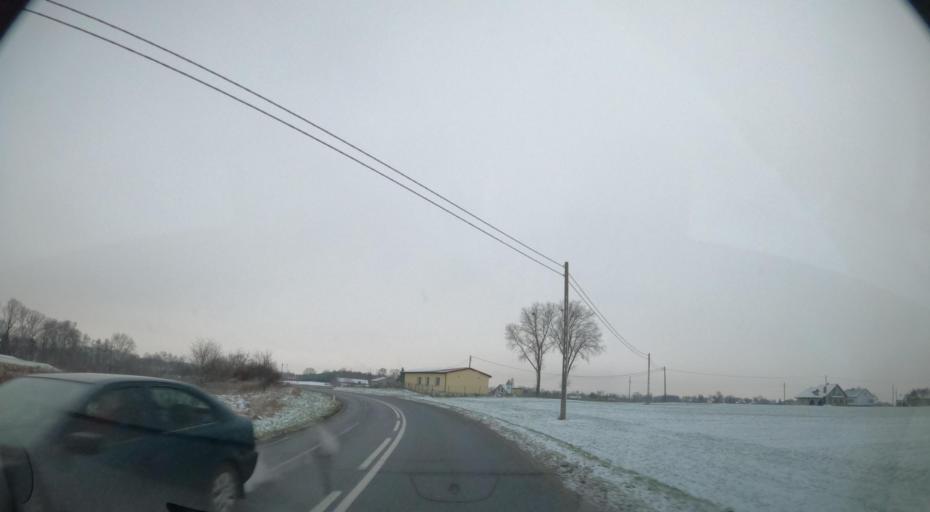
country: PL
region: Kujawsko-Pomorskie
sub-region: Powiat lipnowski
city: Dobrzyn nad Wisla
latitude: 52.6496
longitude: 19.3930
